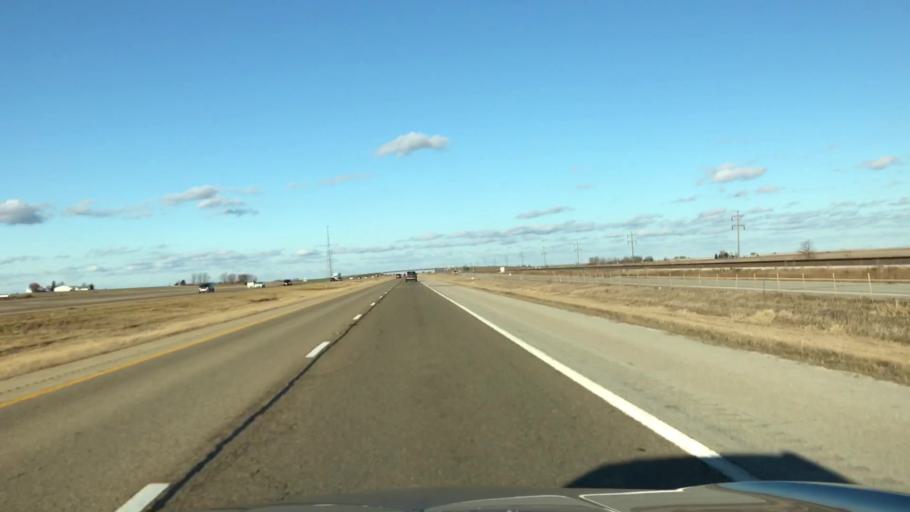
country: US
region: Illinois
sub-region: McLean County
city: Lexington
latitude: 40.6683
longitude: -88.7690
